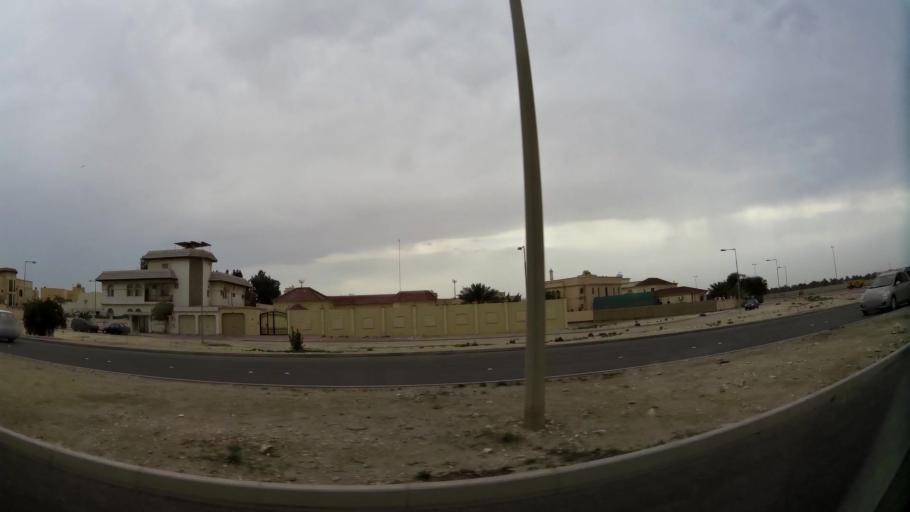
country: BH
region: Central Governorate
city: Madinat Hamad
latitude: 26.1144
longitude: 50.4940
